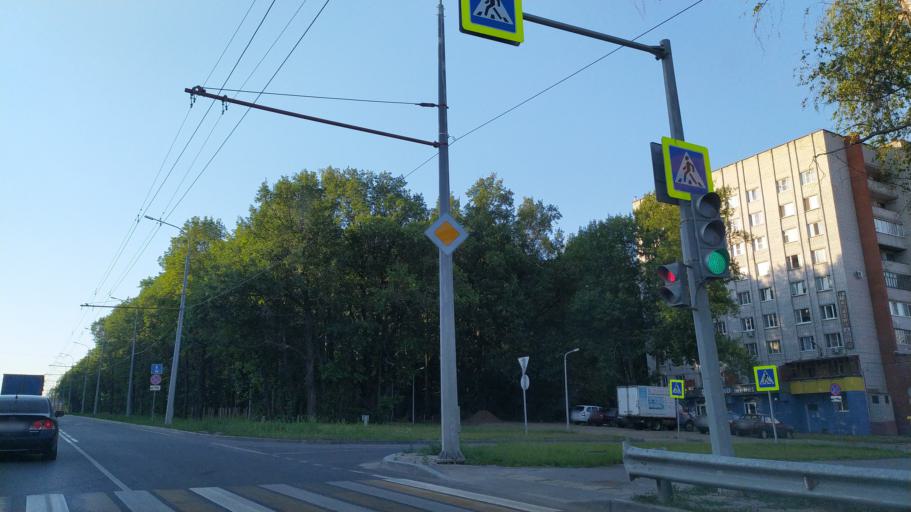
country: RU
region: Chuvashia
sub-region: Cheboksarskiy Rayon
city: Cheboksary
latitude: 56.0896
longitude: 47.2673
